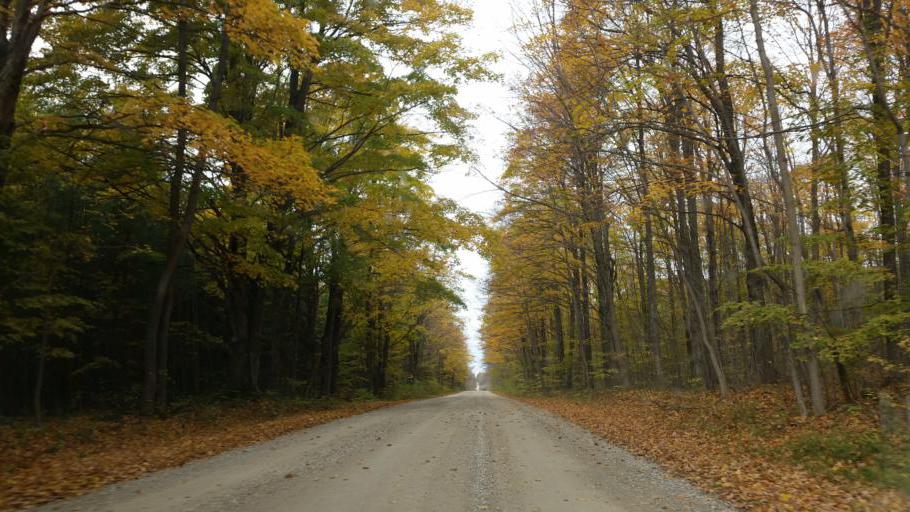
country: CA
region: Ontario
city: Wingham
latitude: 43.9853
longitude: -81.3348
